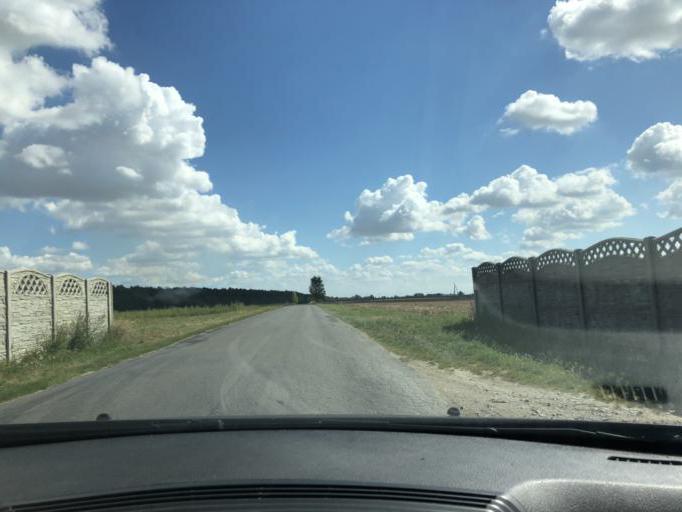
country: PL
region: Lodz Voivodeship
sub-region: Powiat wieruszowski
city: Czastary
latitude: 51.2597
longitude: 18.3365
